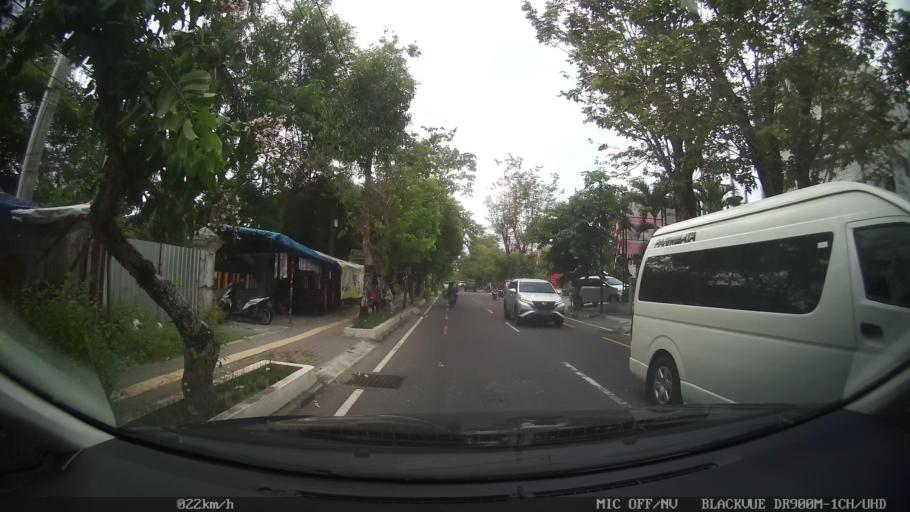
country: ID
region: Daerah Istimewa Yogyakarta
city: Yogyakarta
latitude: -7.7988
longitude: 110.3923
